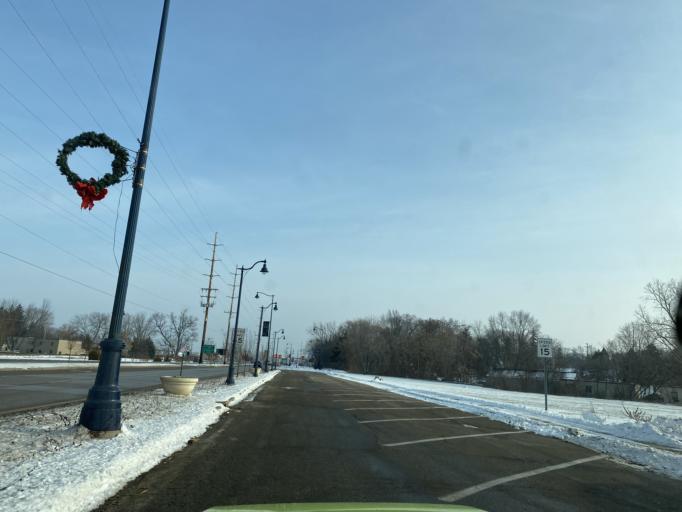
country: US
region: Michigan
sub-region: Ottawa County
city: Hudsonville
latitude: 42.8687
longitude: -85.8645
